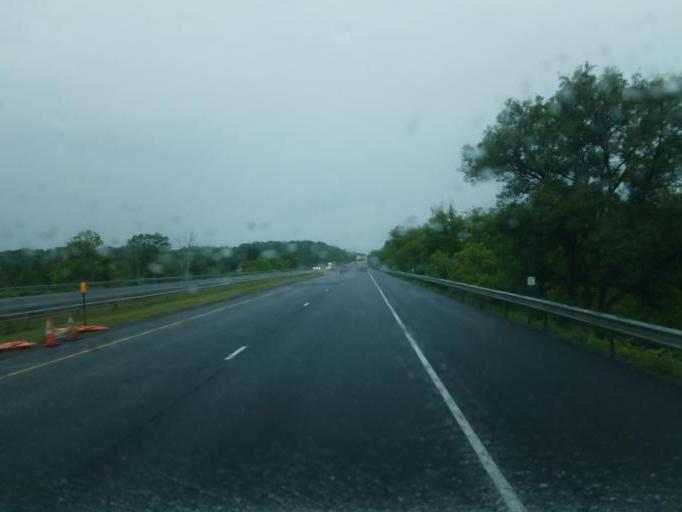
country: US
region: New York
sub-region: Oneida County
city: Whitesboro
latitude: 43.1327
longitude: -75.2929
